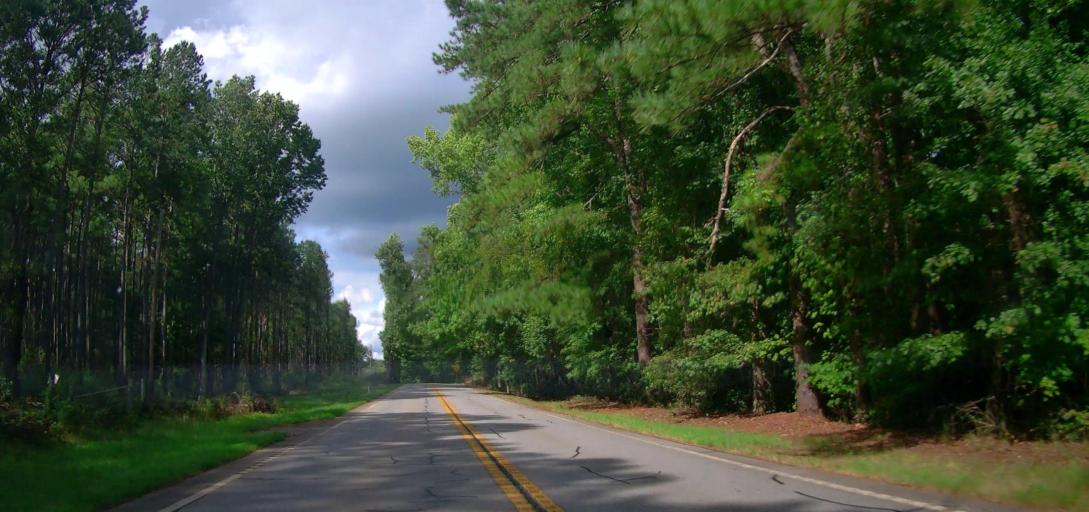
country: US
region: Georgia
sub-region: Harris County
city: Hamilton
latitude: 32.6853
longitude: -84.8574
